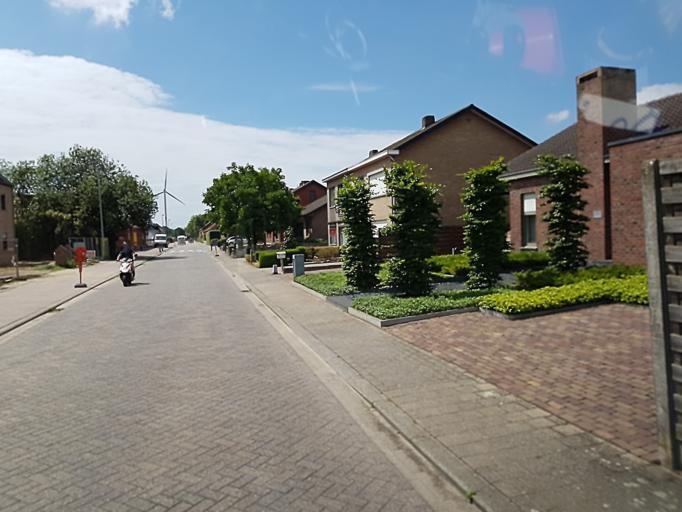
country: BE
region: Flanders
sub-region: Provincie Antwerpen
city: Geel
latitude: 51.1433
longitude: 4.9458
